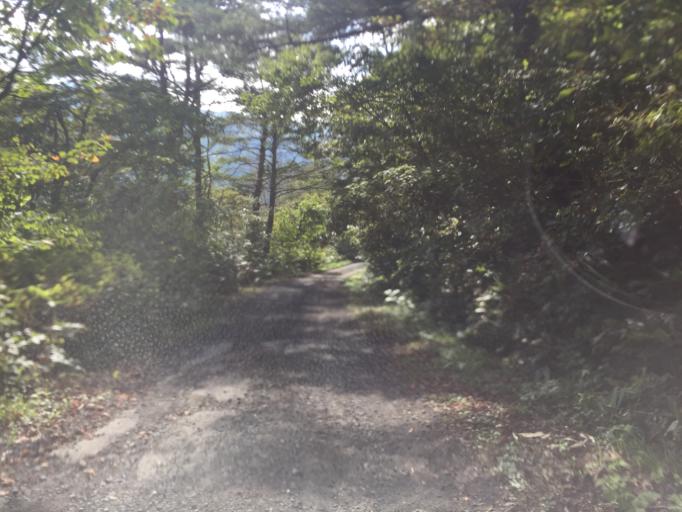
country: JP
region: Yamagata
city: Yonezawa
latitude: 37.8198
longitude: 140.2412
